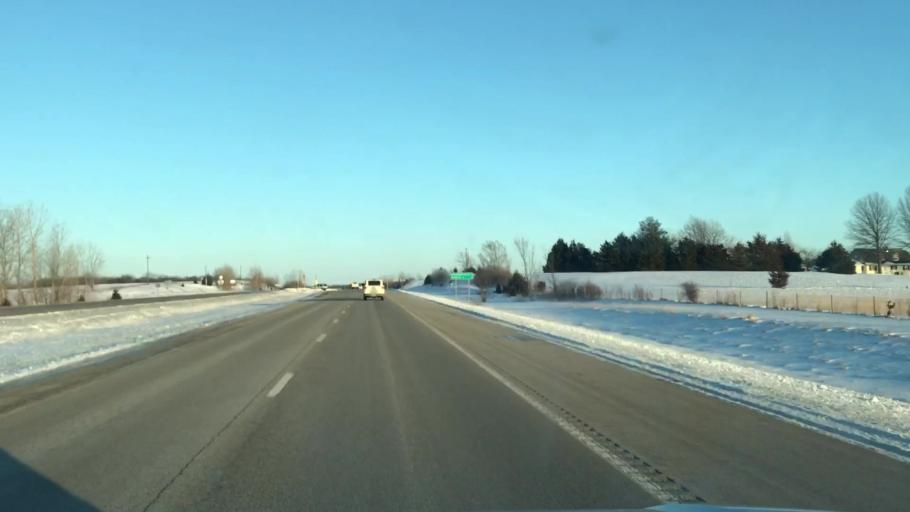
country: US
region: Missouri
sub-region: Clinton County
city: Gower
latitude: 39.7470
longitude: -94.6156
